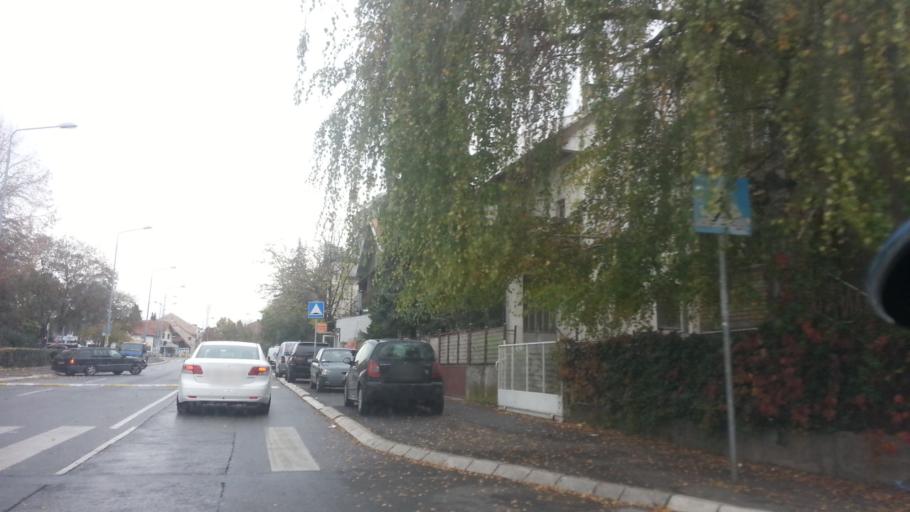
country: RS
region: Central Serbia
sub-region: Belgrade
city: Zemun
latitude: 44.8443
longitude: 20.3948
